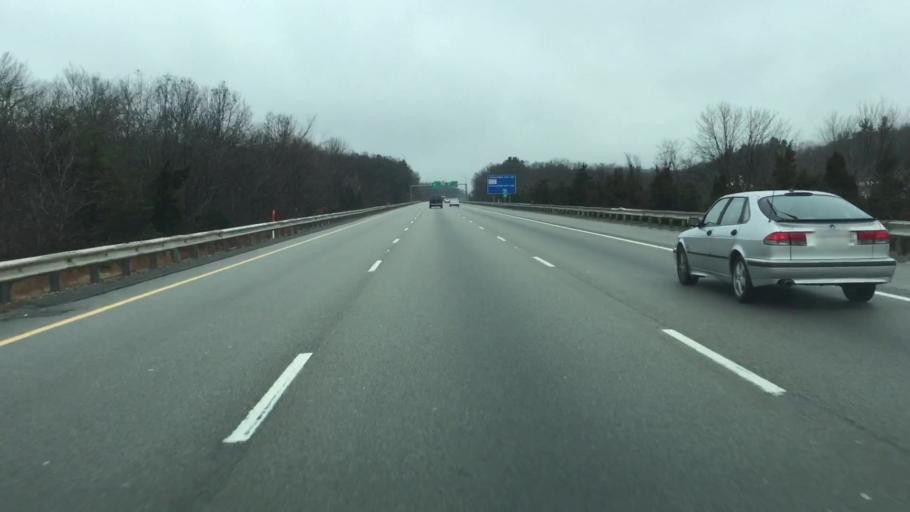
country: US
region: Massachusetts
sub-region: Worcester County
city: Cordaville
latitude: 42.2812
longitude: -71.5659
